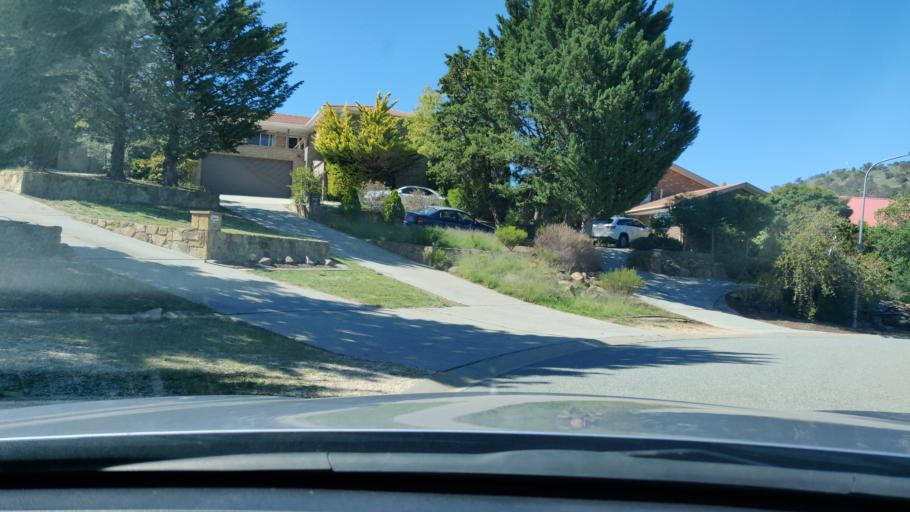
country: AU
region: Australian Capital Territory
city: Macarthur
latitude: -35.4411
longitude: 149.1020
